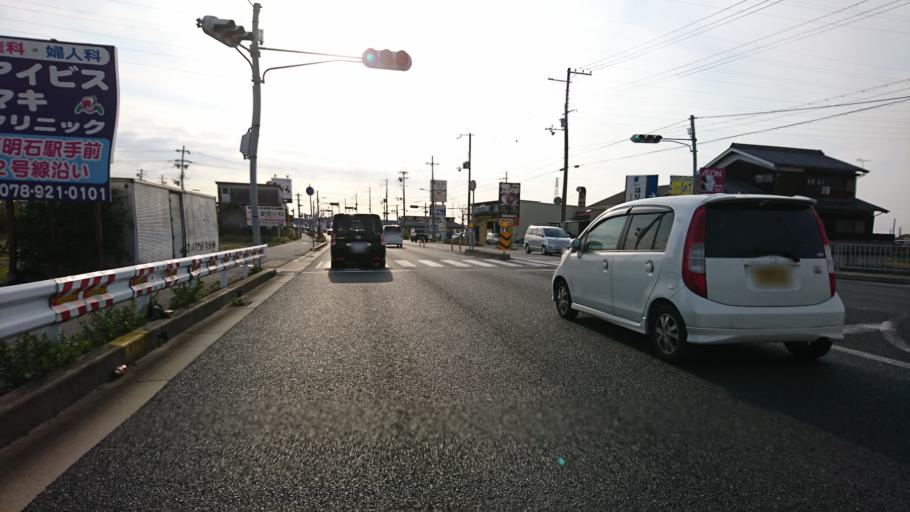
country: JP
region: Hyogo
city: Kakogawacho-honmachi
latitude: 34.7138
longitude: 134.8859
